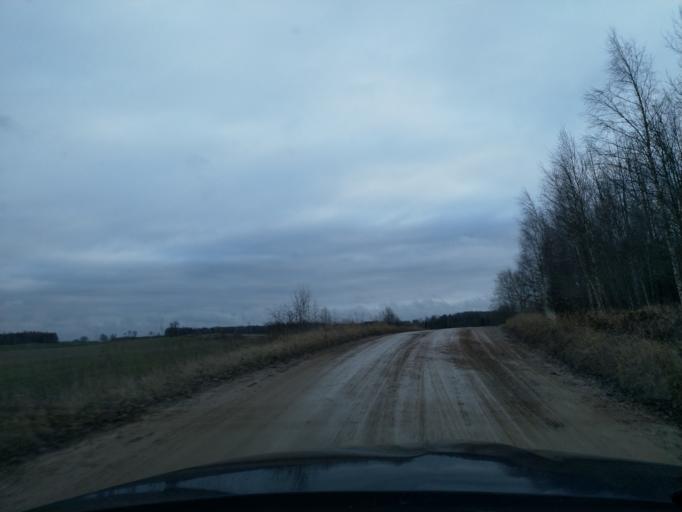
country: LV
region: Saldus Rajons
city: Saldus
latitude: 56.8930
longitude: 22.2690
